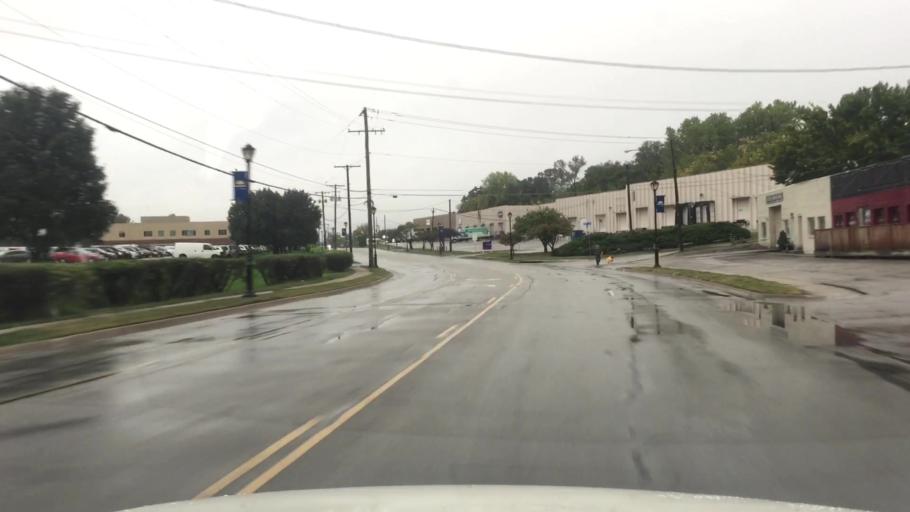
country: US
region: Kansas
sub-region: Johnson County
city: Merriam
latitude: 39.0337
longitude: -94.6909
